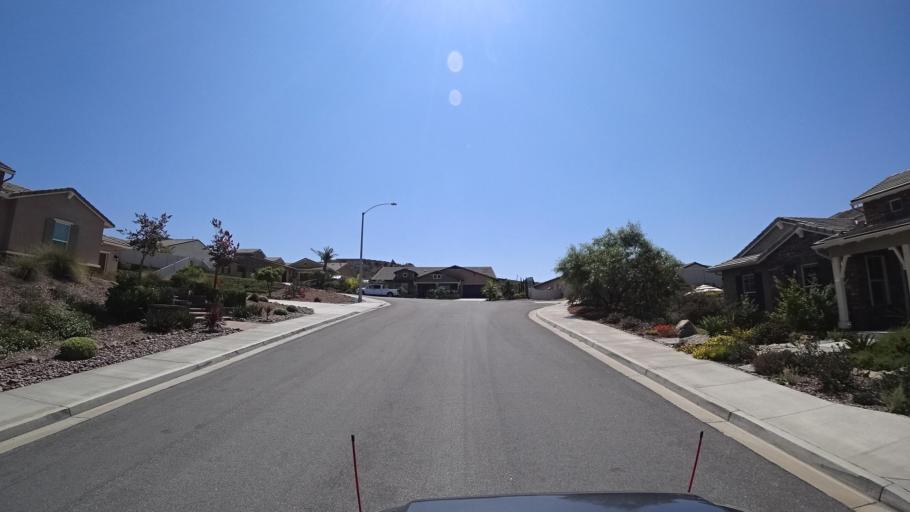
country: US
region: California
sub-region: San Diego County
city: San Marcos
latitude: 33.1804
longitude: -117.1950
